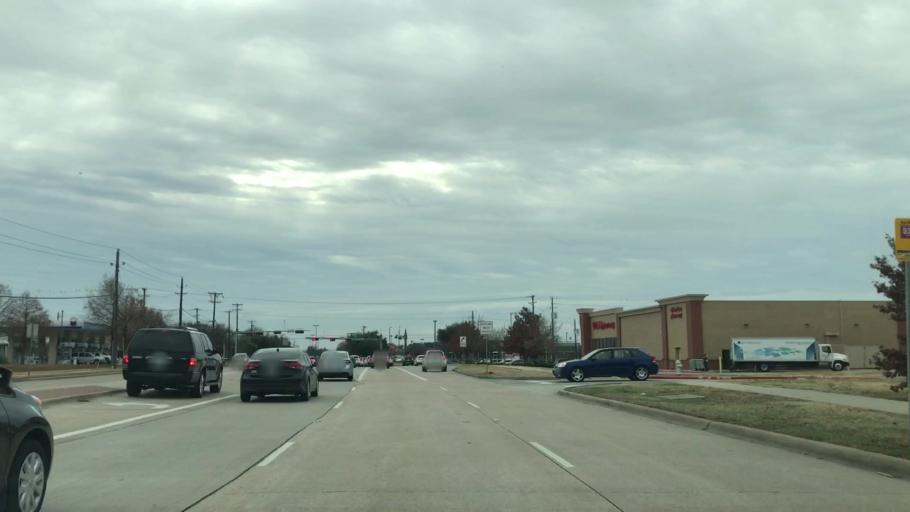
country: US
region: Texas
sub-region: Denton County
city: The Colony
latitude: 33.0264
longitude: -96.8850
